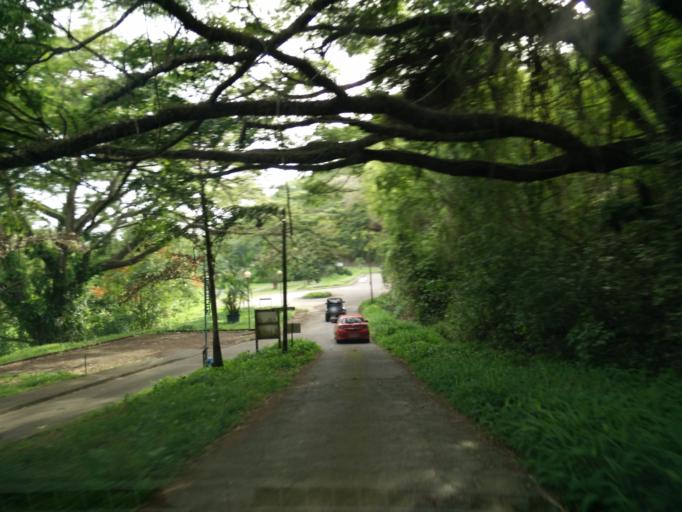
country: MQ
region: Martinique
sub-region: Martinique
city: Saint-Pierre
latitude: 14.7159
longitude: -61.1680
